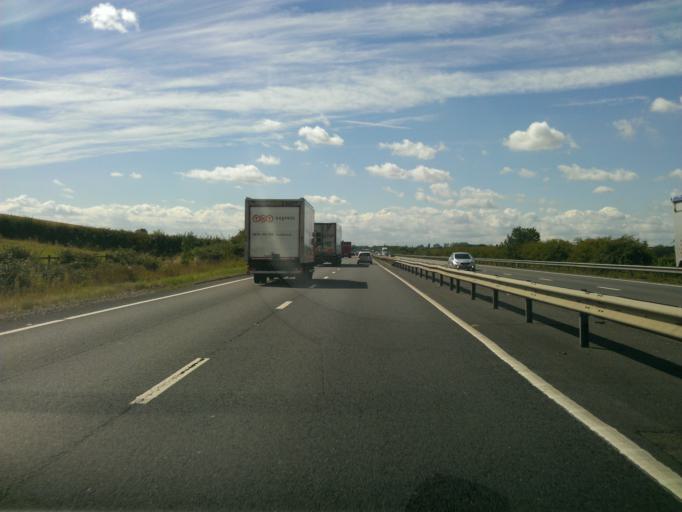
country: GB
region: England
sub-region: Bedford
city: Pertenhall
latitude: 52.3618
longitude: -0.4143
